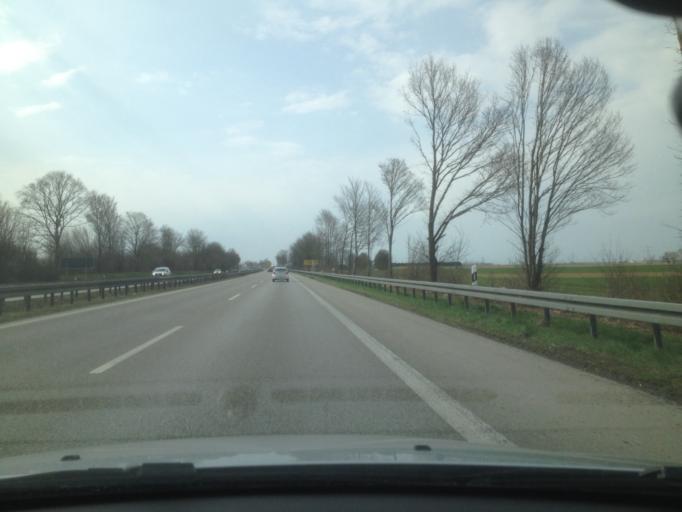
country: DE
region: Bavaria
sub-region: Swabia
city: Konigsbrunn
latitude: 48.2723
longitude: 10.8682
